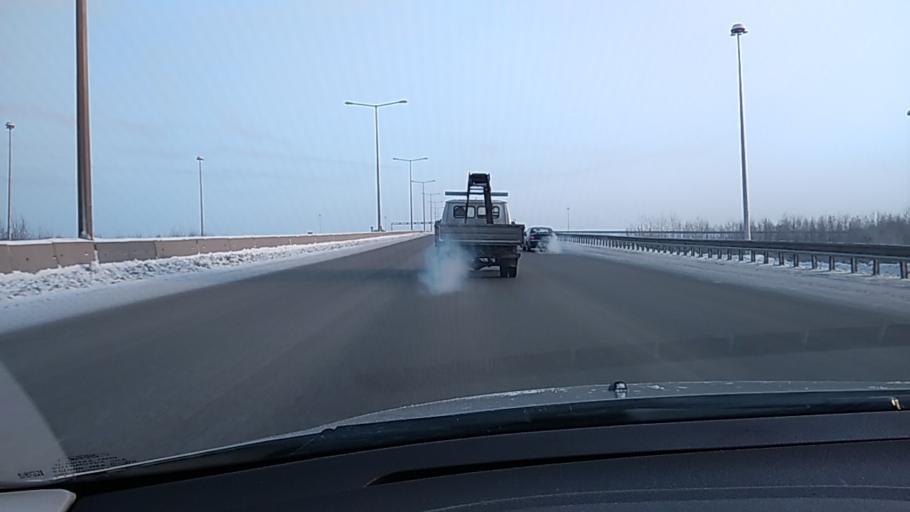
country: RU
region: Sverdlovsk
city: Istok
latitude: 56.7620
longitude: 60.7622
